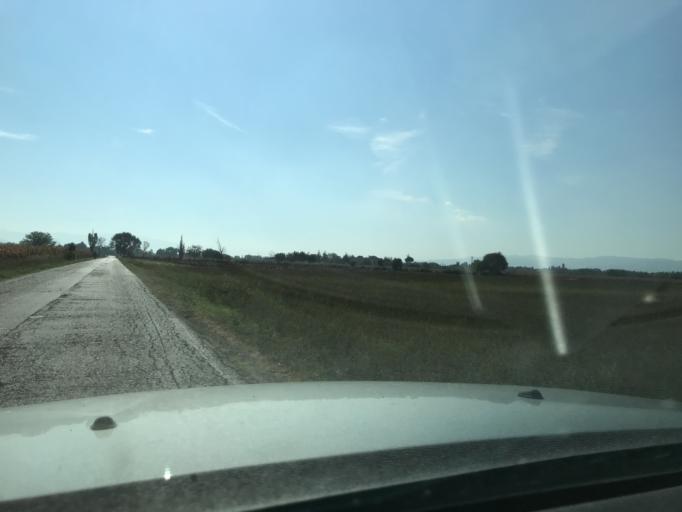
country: IT
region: Umbria
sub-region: Provincia di Perugia
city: Ospedalicchio
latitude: 43.0901
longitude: 12.5028
